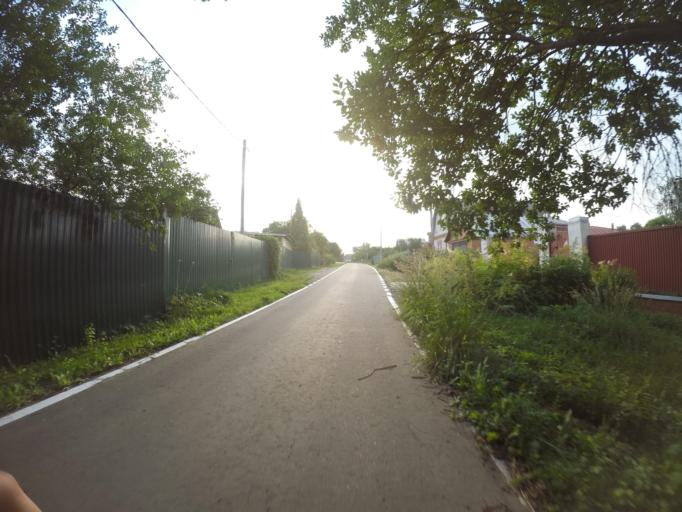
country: RU
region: Moskovskaya
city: Rechitsy
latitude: 55.5965
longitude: 38.5067
